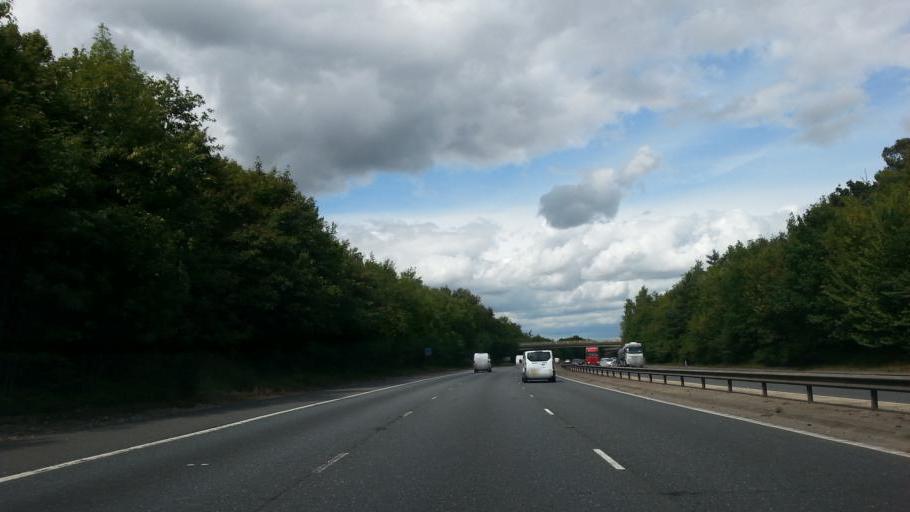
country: GB
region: England
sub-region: Essex
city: Little Hallingbury
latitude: 51.8477
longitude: 0.1855
